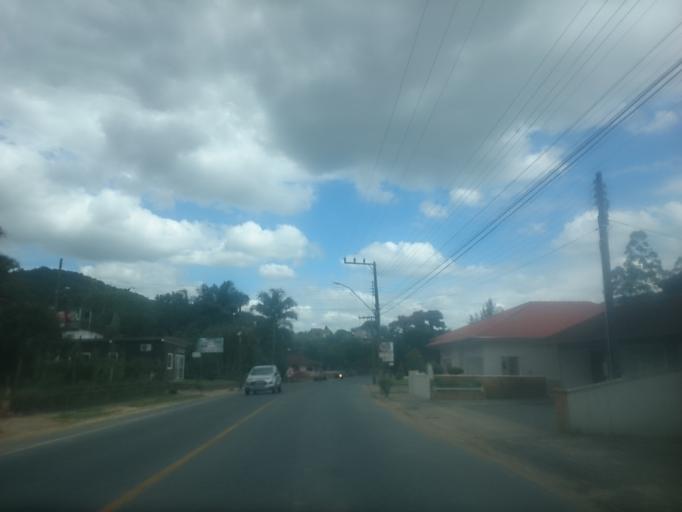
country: BR
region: Santa Catarina
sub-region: Pomerode
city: Pomerode
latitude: -26.7209
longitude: -49.1677
